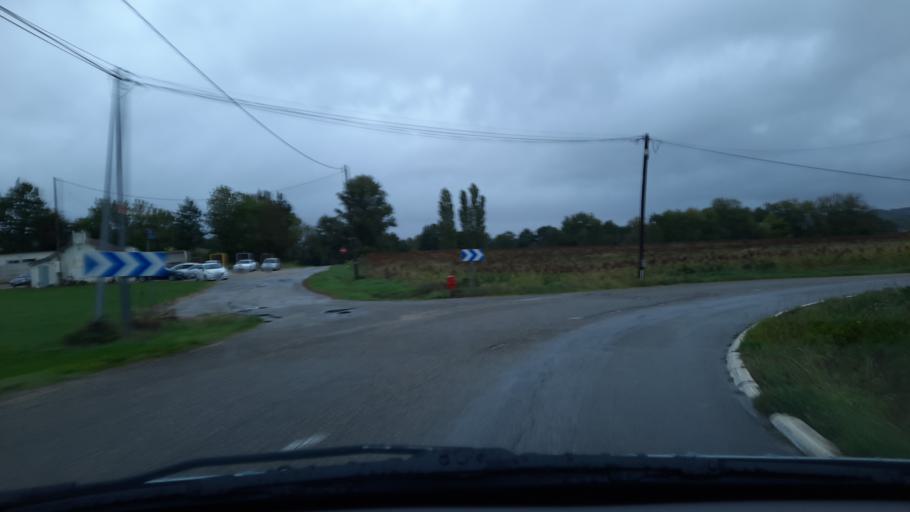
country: FR
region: Midi-Pyrenees
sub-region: Departement du Tarn-et-Garonne
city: Lafrancaise
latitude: 44.1902
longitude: 1.2790
